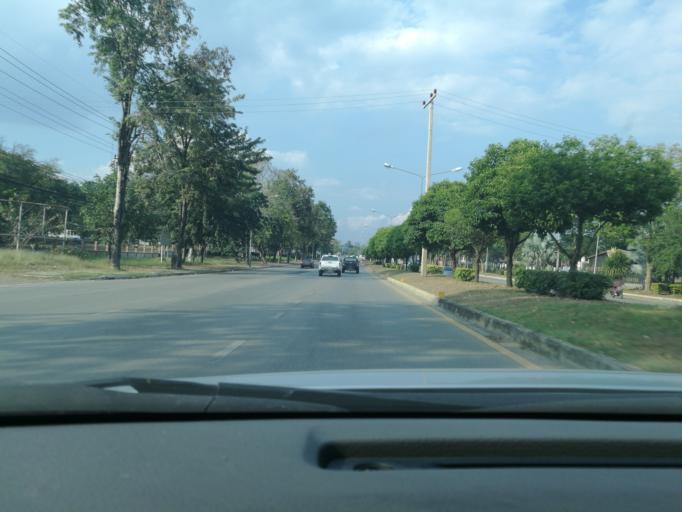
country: TH
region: Phetchabun
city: Phetchabun
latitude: 16.4379
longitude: 101.1518
